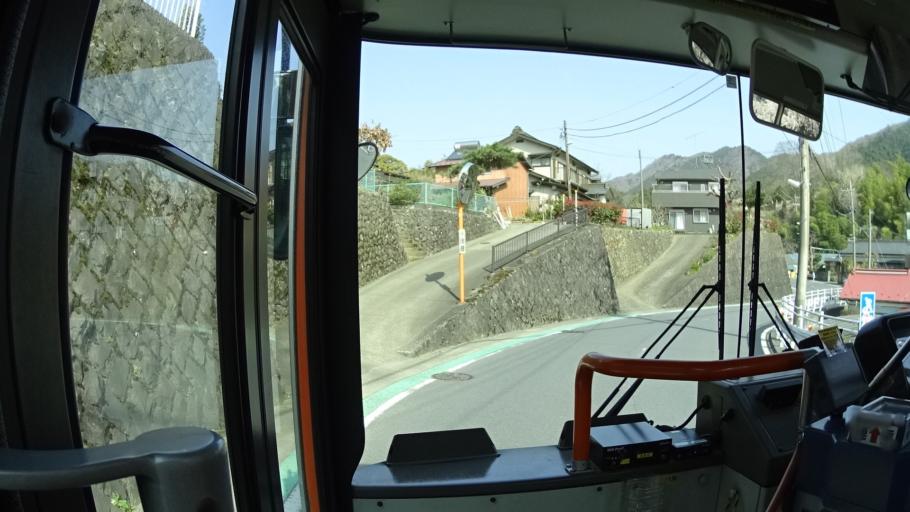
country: JP
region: Kanagawa
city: Atsugi
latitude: 35.4870
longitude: 139.2719
